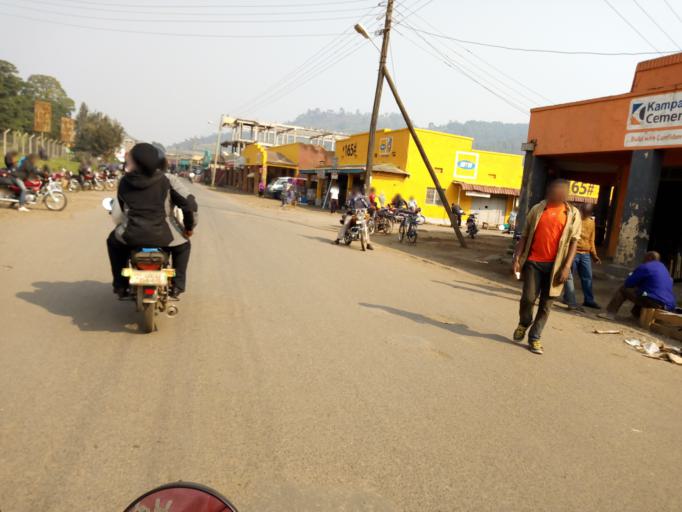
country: UG
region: Western Region
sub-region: Kisoro District
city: Kisoro
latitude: -1.2819
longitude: 29.6942
